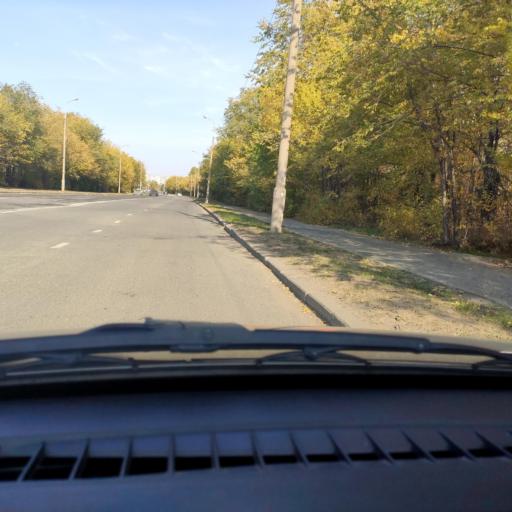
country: RU
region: Samara
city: Tol'yatti
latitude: 53.5030
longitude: 49.2514
